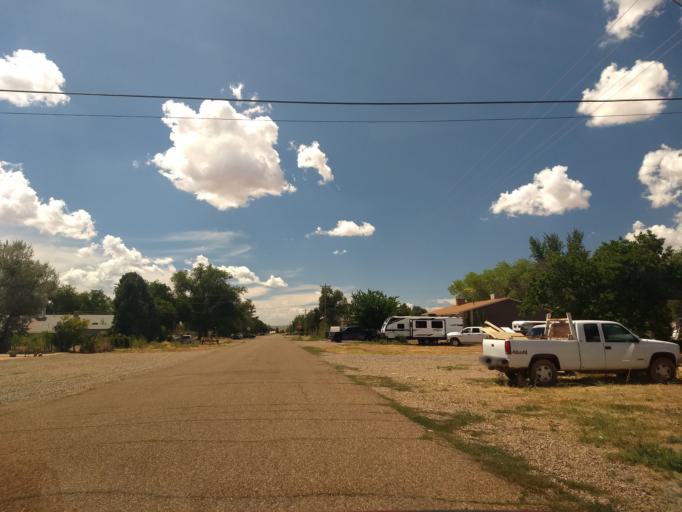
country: US
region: Arizona
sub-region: Coconino County
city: Fredonia
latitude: 36.9518
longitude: -112.5243
